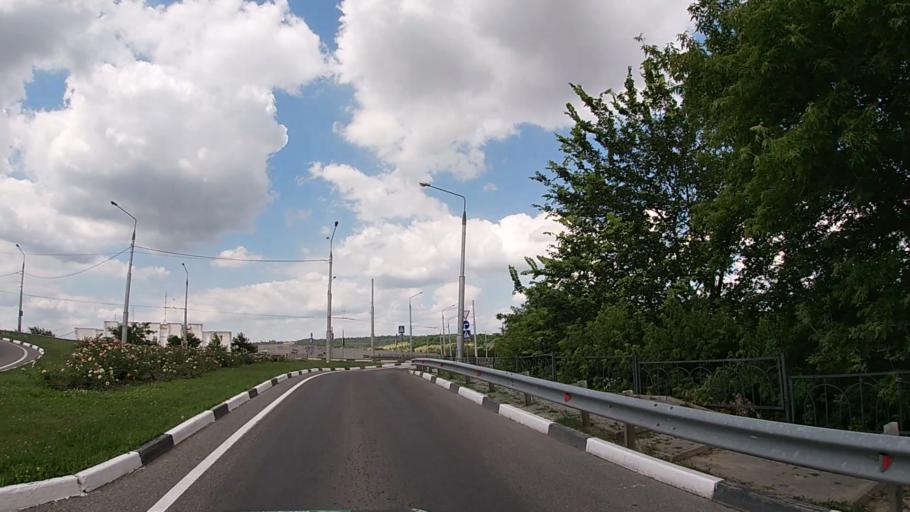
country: RU
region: Belgorod
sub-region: Belgorodskiy Rayon
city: Belgorod
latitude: 50.5898
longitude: 36.5665
